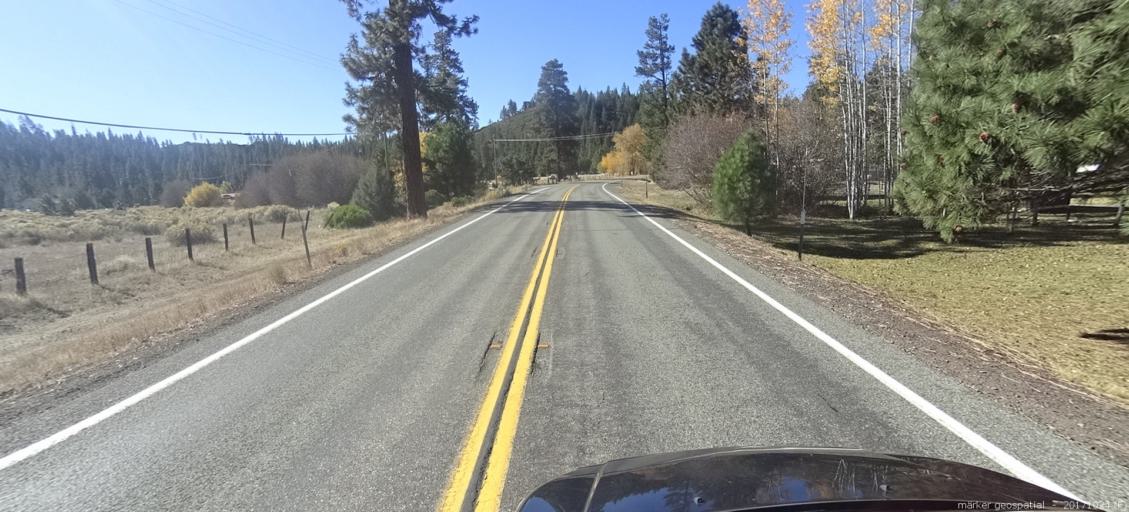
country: US
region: California
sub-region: Shasta County
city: Burney
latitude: 40.6759
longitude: -121.4299
